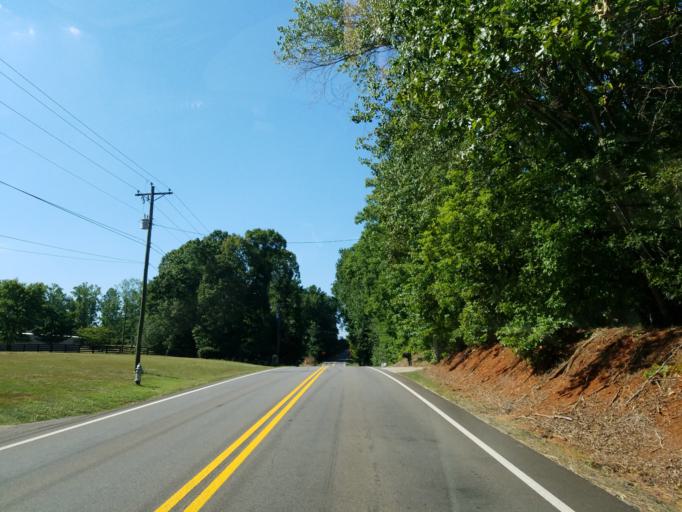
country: US
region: Georgia
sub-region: Fulton County
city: Milton
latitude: 34.2222
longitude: -84.2897
